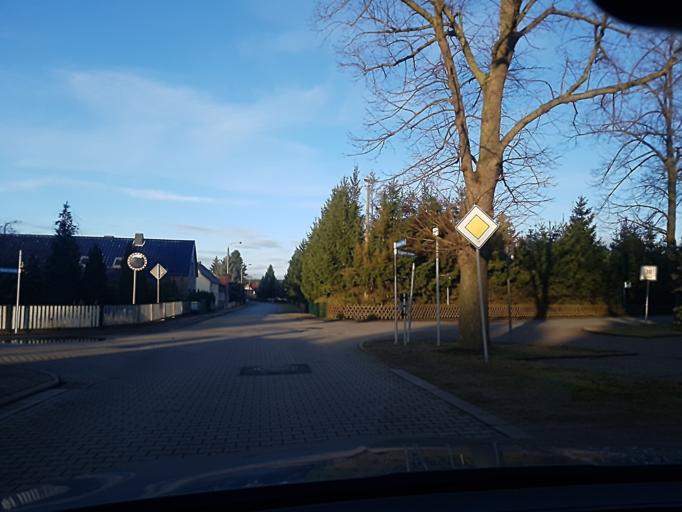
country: DE
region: Brandenburg
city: Schilda
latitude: 51.6035
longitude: 13.3878
